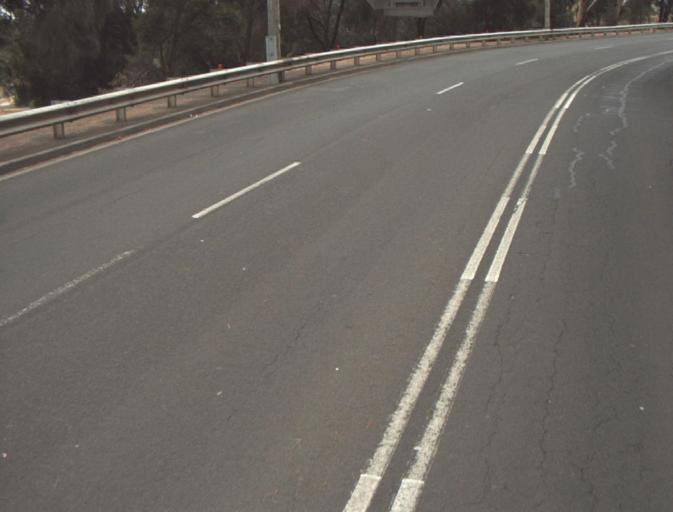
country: AU
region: Tasmania
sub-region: Launceston
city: Newstead
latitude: -41.4375
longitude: 147.1814
